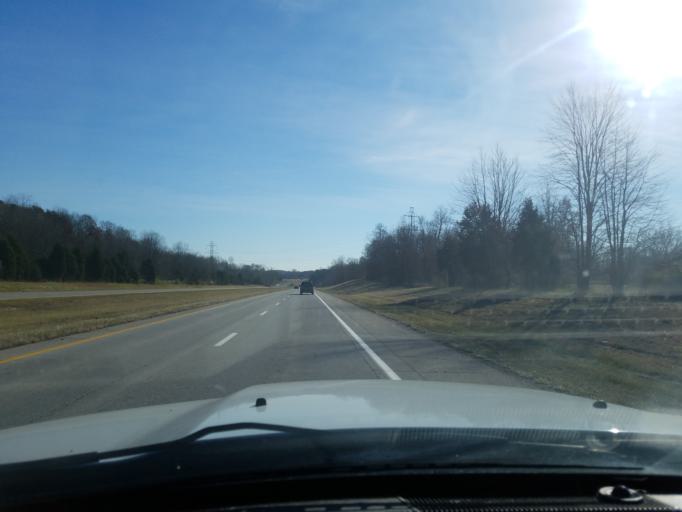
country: US
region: Ohio
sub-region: Brown County
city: Mount Orab
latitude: 39.0256
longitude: -83.8764
